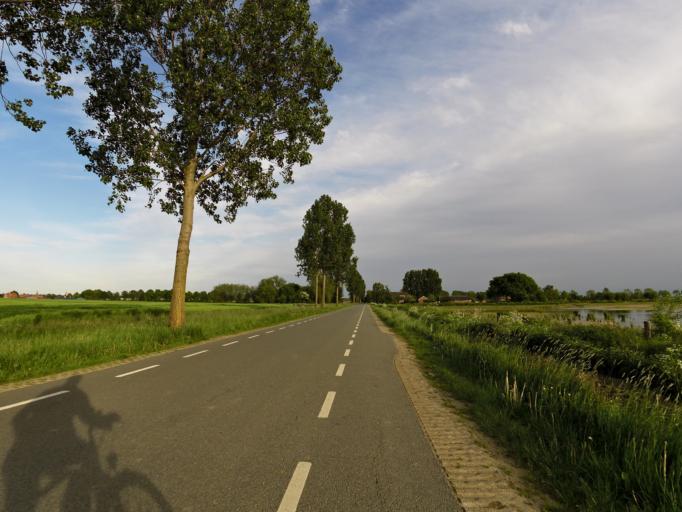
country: NL
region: Gelderland
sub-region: Oude IJsselstreek
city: Gendringen
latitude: 51.8749
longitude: 6.3448
